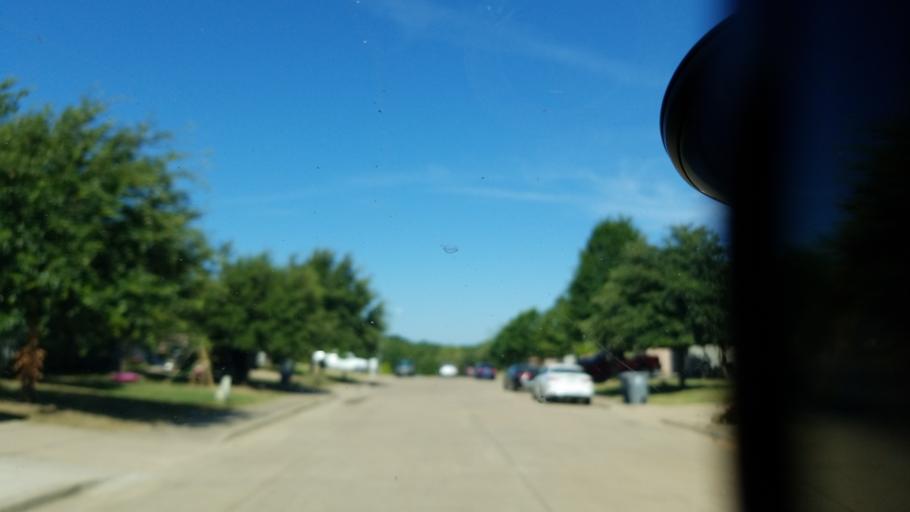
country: US
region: Texas
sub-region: Dallas County
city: Cockrell Hill
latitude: 32.6769
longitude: -96.8249
